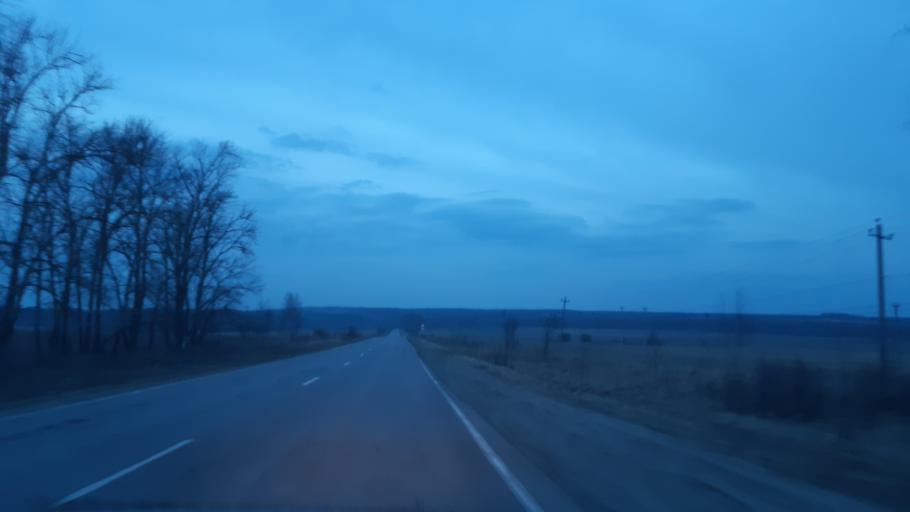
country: RU
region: Vladimir
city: Nikologory
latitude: 56.1648
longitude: 41.9973
